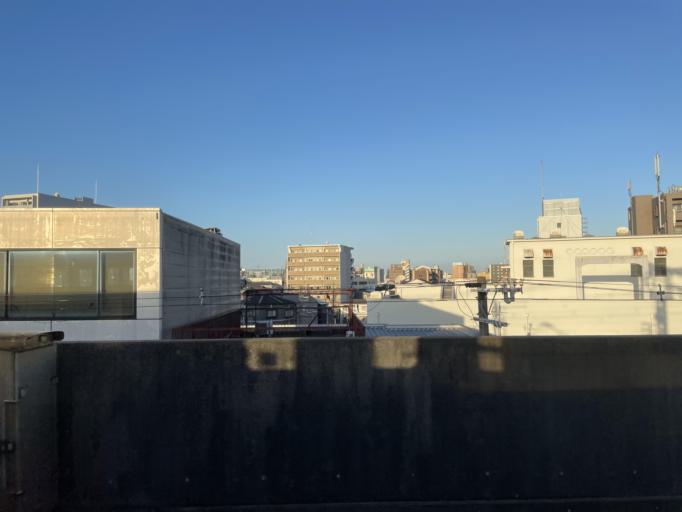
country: JP
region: Osaka
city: Osaka-shi
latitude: 34.6368
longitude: 135.5272
